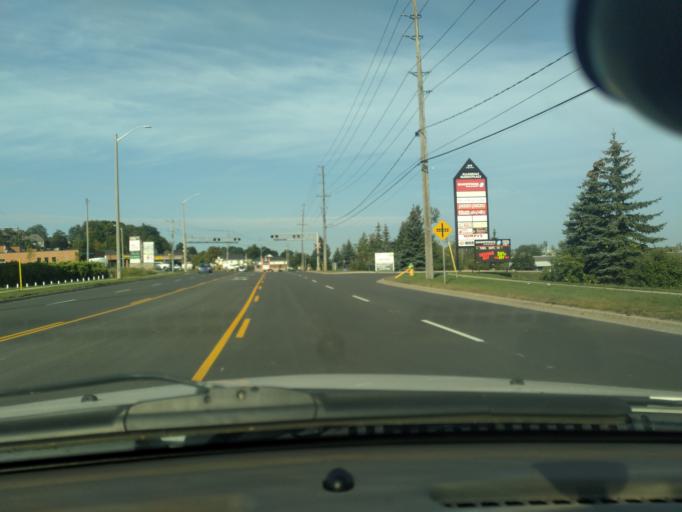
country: CA
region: Ontario
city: Barrie
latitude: 44.3706
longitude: -79.6717
